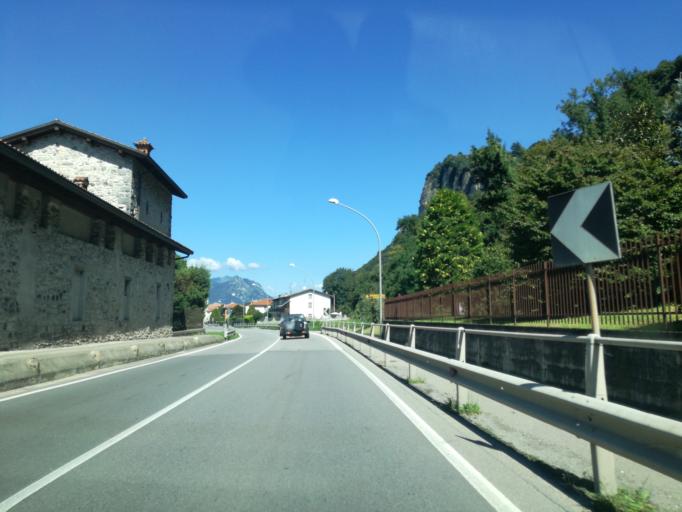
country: IT
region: Lombardy
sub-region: Provincia di Lecco
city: Monte Marenzo
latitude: 45.7587
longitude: 9.4530
